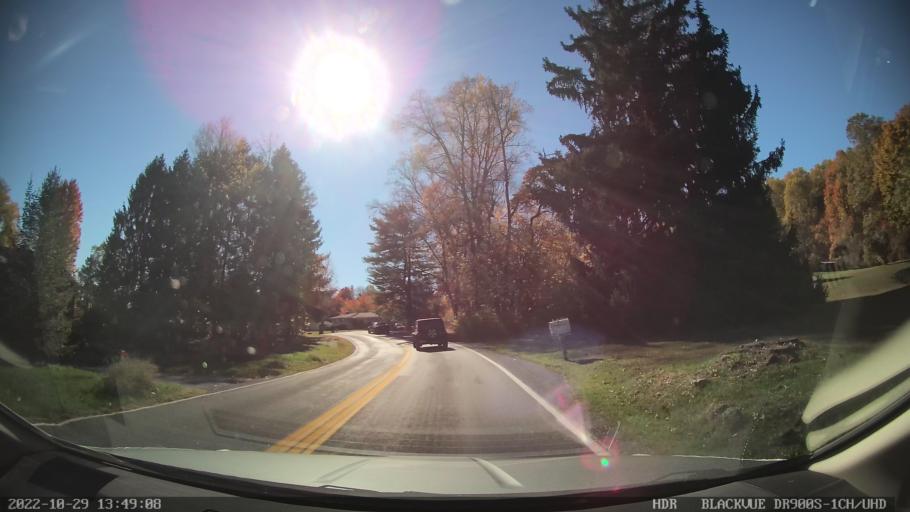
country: US
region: Pennsylvania
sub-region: Lehigh County
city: Emmaus
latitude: 40.5435
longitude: -75.4550
